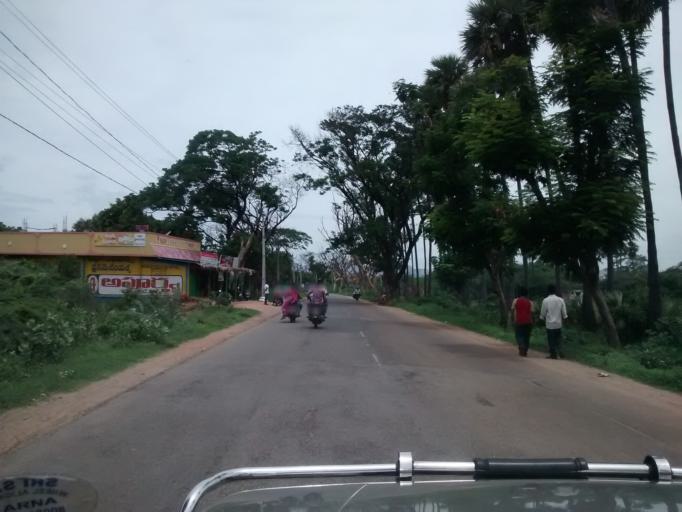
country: IN
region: Andhra Pradesh
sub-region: Chittoor
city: Narasingapuram
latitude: 13.6133
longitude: 79.3605
